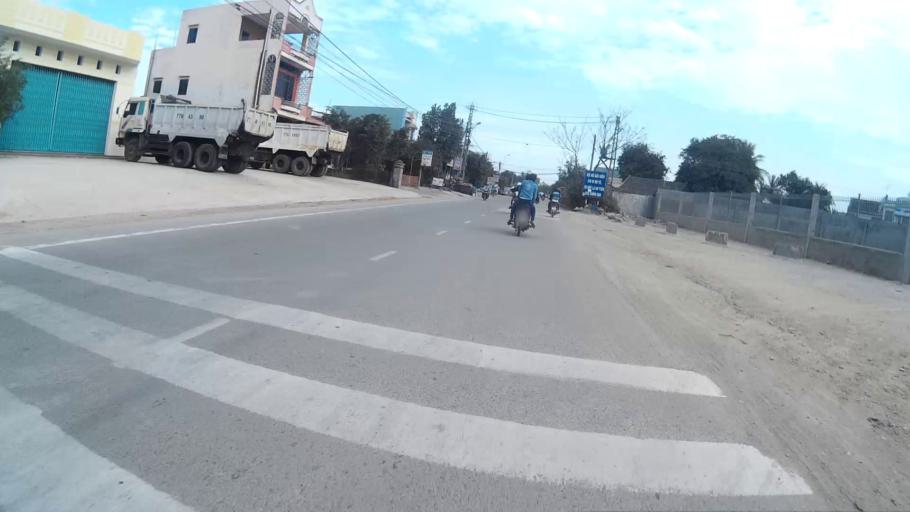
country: VN
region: Binh Dinh
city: An Nhon
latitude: 13.8632
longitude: 109.1325
